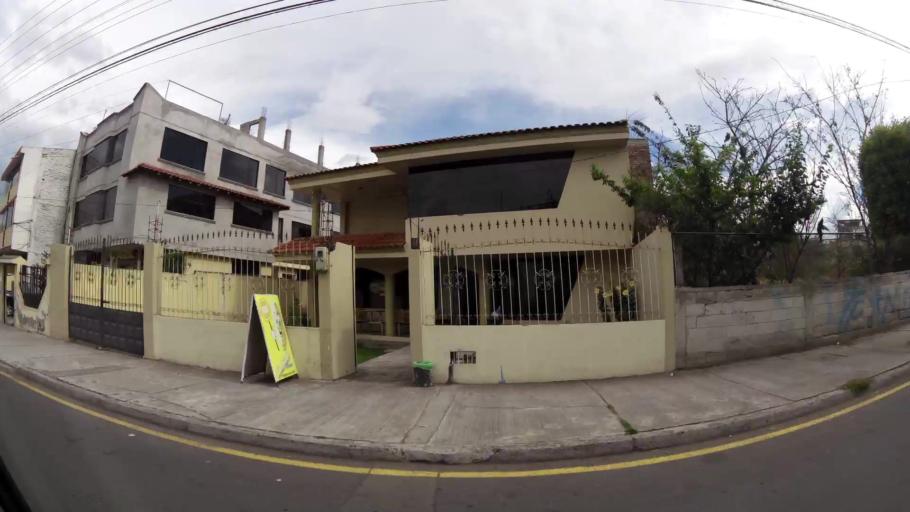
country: EC
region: Tungurahua
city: Ambato
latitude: -1.2705
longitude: -78.6377
